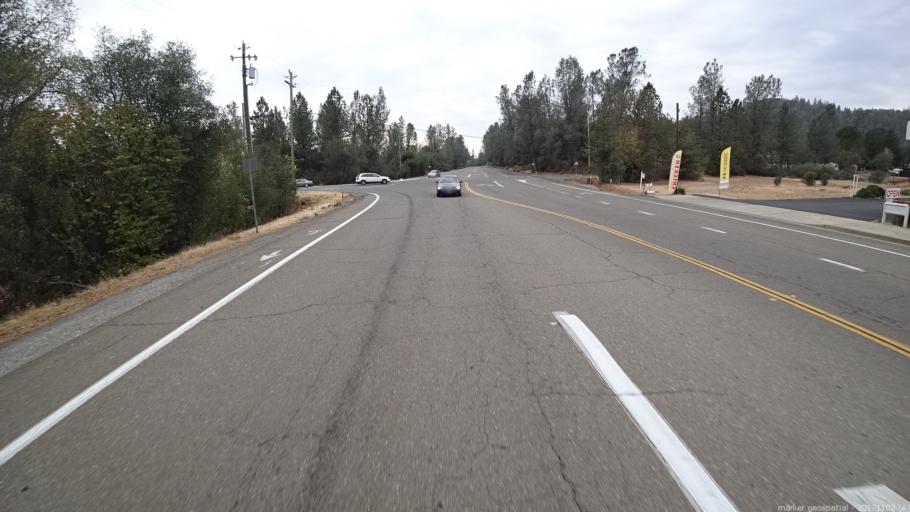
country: US
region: California
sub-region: Shasta County
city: Central Valley (historical)
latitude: 40.6633
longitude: -122.3963
